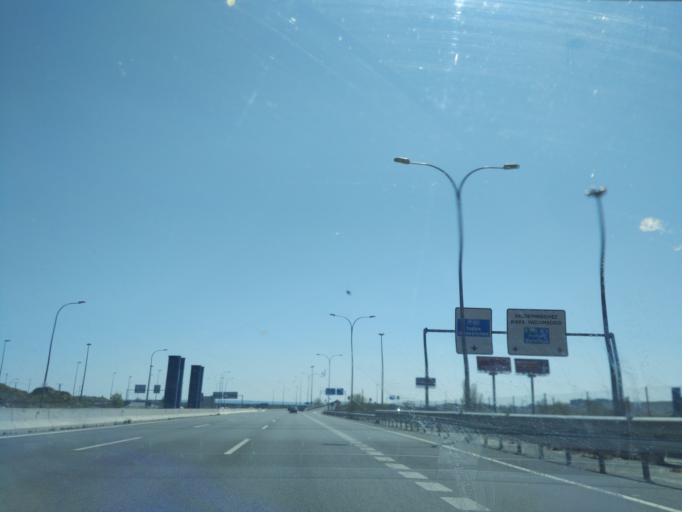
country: ES
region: Madrid
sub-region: Provincia de Madrid
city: Villa de Vallecas
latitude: 40.3633
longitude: -3.5727
